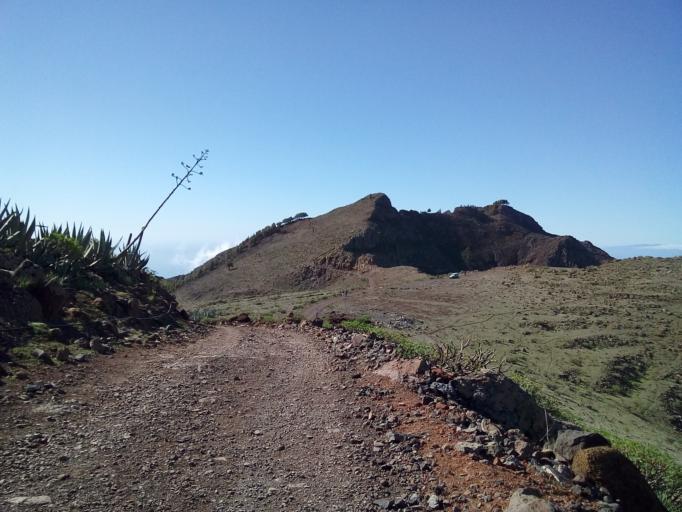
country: ES
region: Canary Islands
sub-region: Provincia de Santa Cruz de Tenerife
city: Vallehermosa
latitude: 28.1245
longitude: -17.3278
